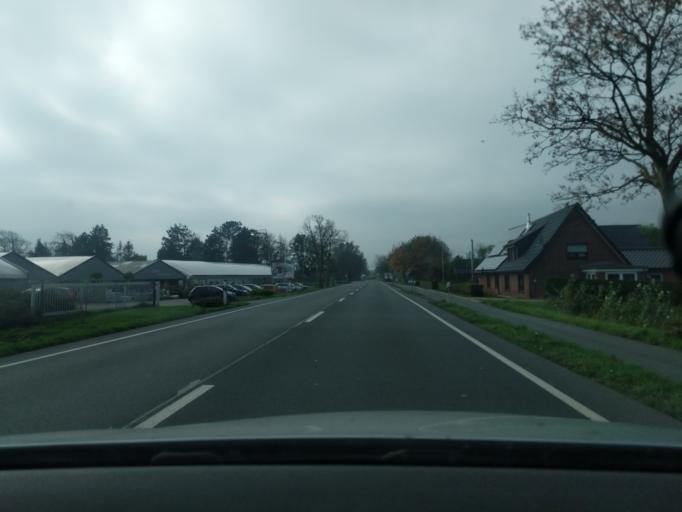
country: DE
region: Lower Saxony
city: Otterndorf
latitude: 53.8174
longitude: 8.9290
